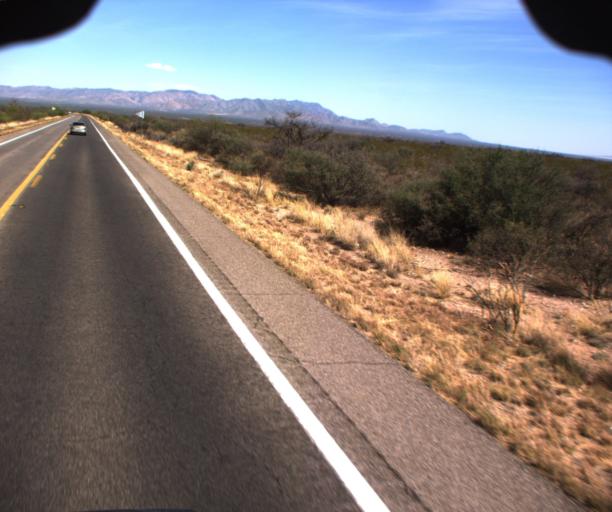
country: US
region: Arizona
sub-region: Cochise County
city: Sierra Vista Southeast
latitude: 31.5470
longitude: -110.1629
